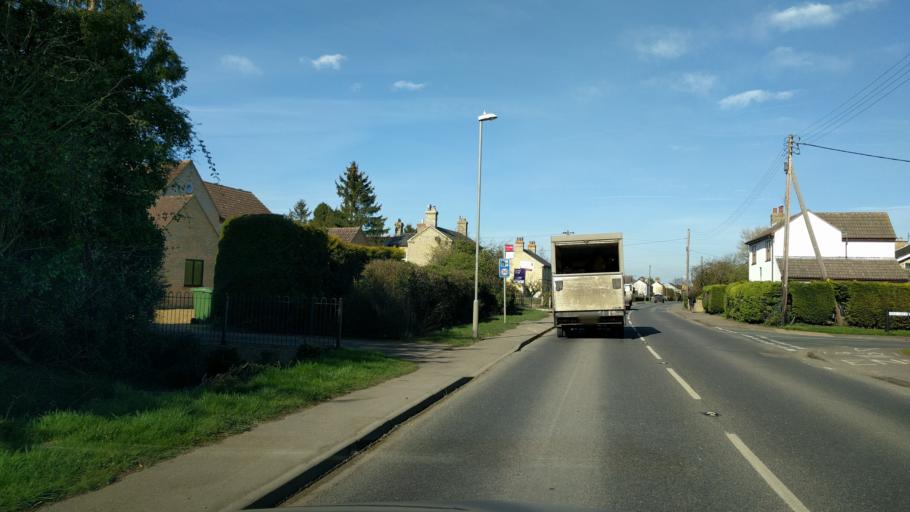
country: GB
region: England
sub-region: Cambridgeshire
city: Earith
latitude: 52.3073
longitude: 0.0531
